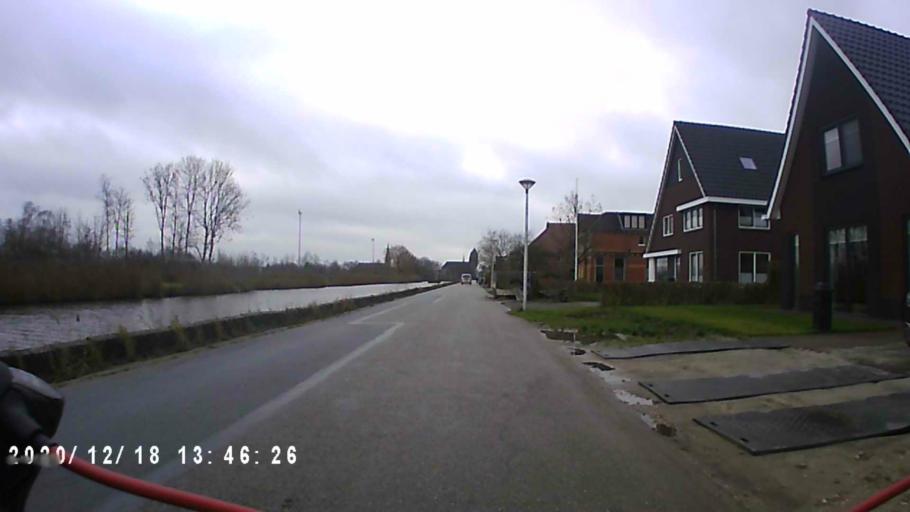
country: NL
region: Groningen
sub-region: Gemeente Bedum
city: Bedum
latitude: 53.3068
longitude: 6.6010
